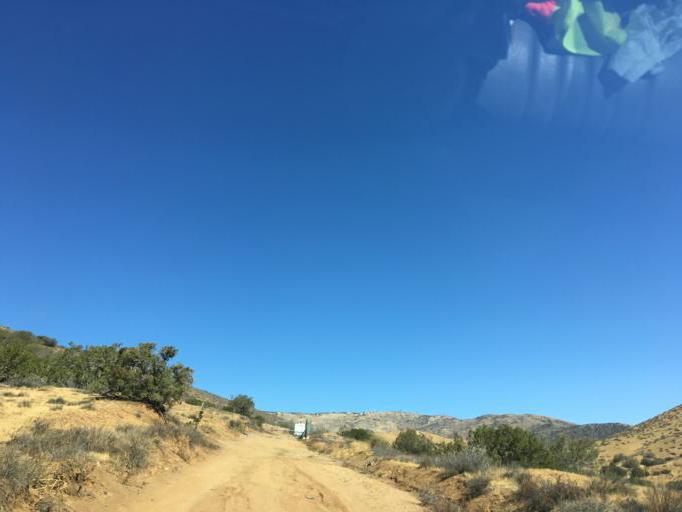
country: US
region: California
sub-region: Los Angeles County
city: Acton
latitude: 34.5084
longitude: -118.2047
